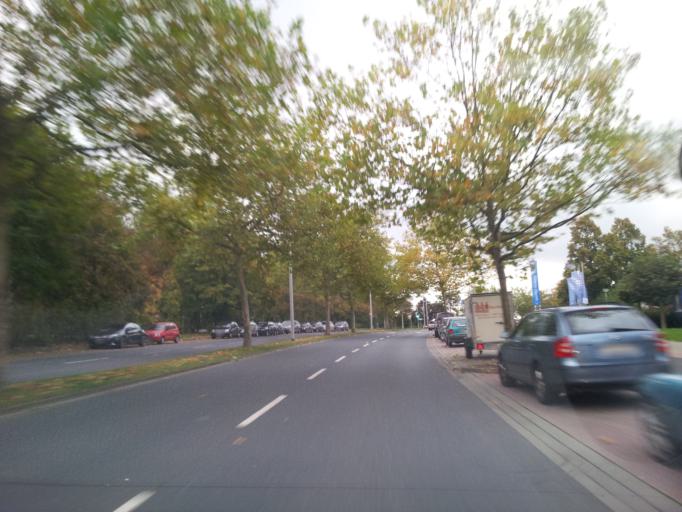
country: DE
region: Lower Saxony
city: Braunschweig
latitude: 52.2320
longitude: 10.5370
